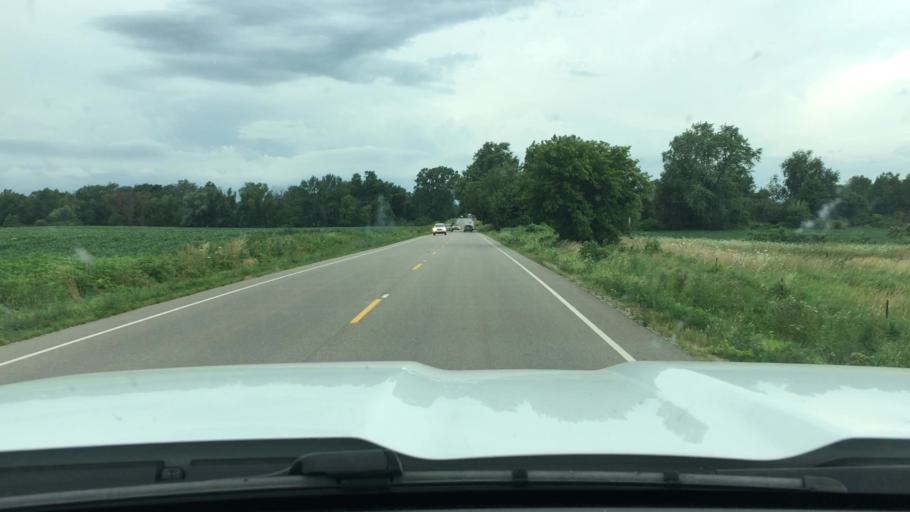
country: US
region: Michigan
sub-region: Kent County
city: Byron Center
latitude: 42.7827
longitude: -85.7948
